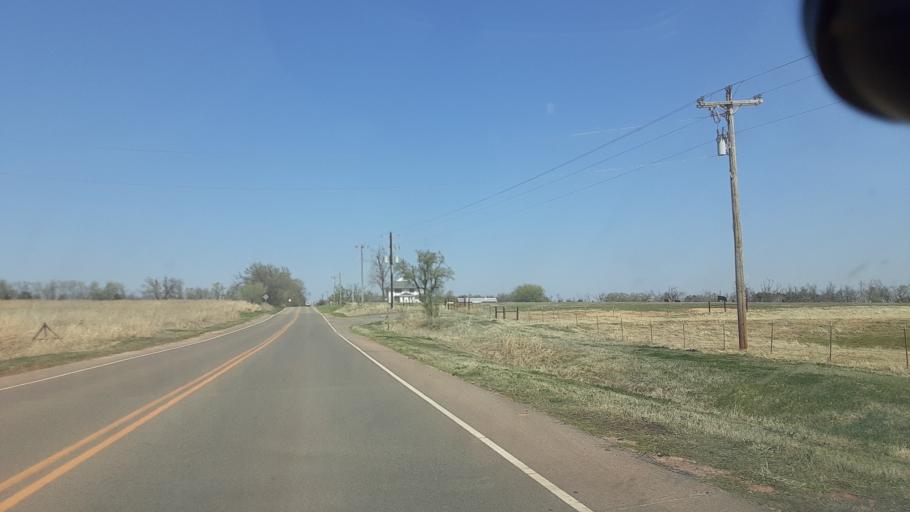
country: US
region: Oklahoma
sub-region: Logan County
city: Guthrie
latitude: 35.8152
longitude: -97.4783
